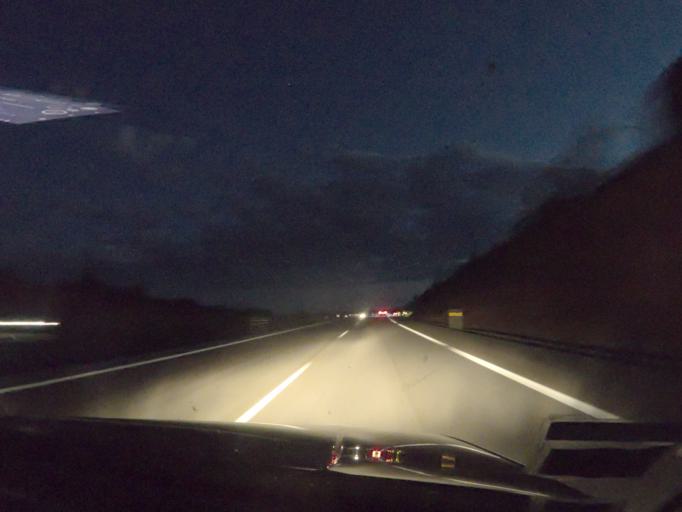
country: ES
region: Castille and Leon
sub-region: Provincia de Leon
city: Brazuelo
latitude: 42.5068
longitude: -6.1174
